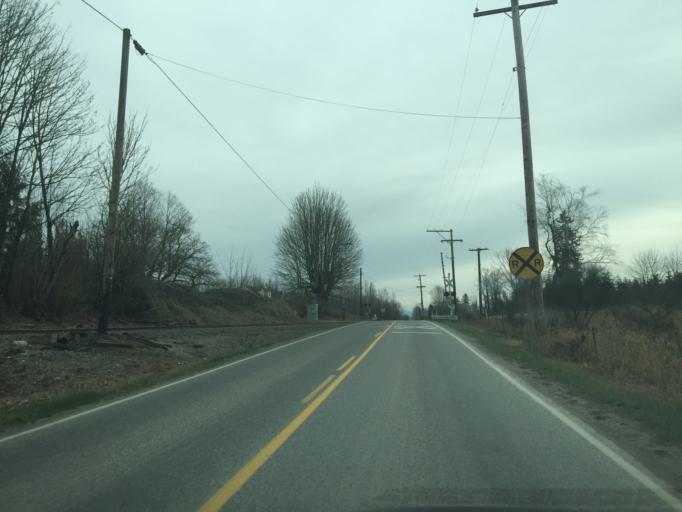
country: US
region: Washington
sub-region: Whatcom County
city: Nooksack
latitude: 48.9721
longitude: -122.3311
